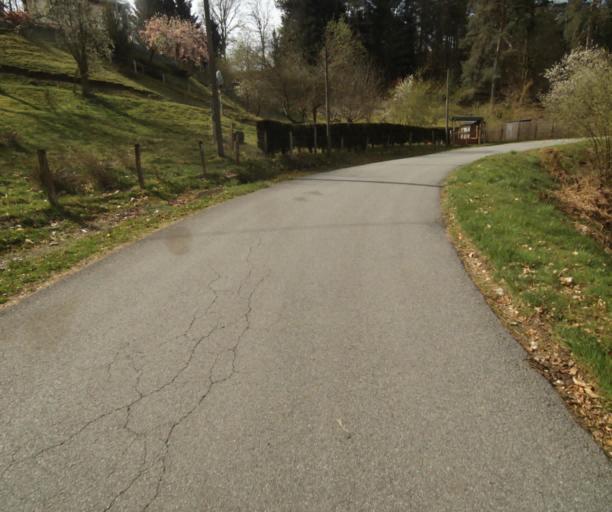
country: FR
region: Limousin
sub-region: Departement de la Correze
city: Correze
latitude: 45.3699
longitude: 1.8809
